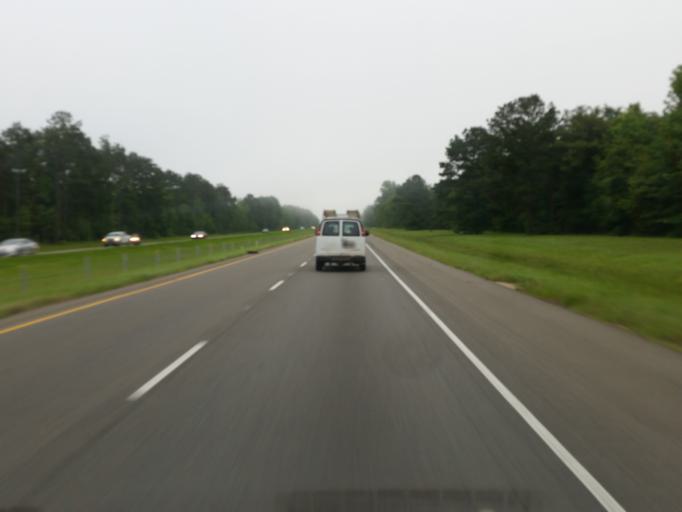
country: US
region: Louisiana
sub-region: Bossier Parish
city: Haughton
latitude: 32.5769
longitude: -93.4628
